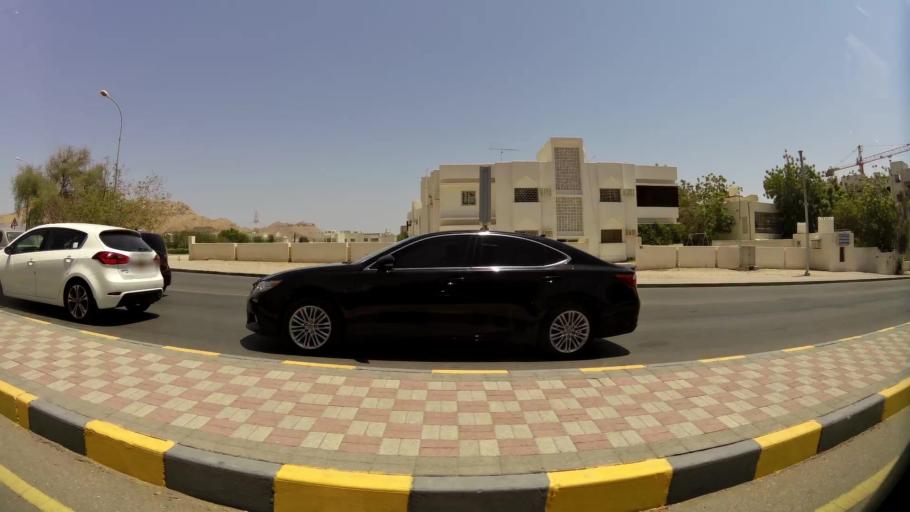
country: OM
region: Muhafazat Masqat
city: Muscat
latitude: 23.6038
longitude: 58.5375
